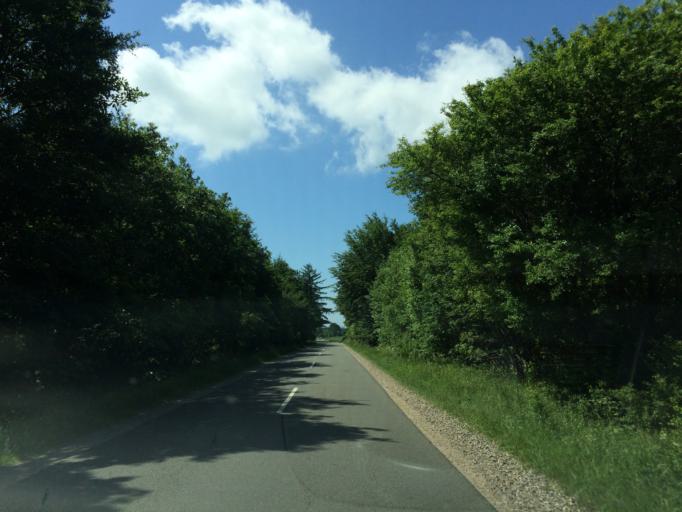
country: DK
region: Central Jutland
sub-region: Holstebro Kommune
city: Ulfborg
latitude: 56.2036
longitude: 8.4597
